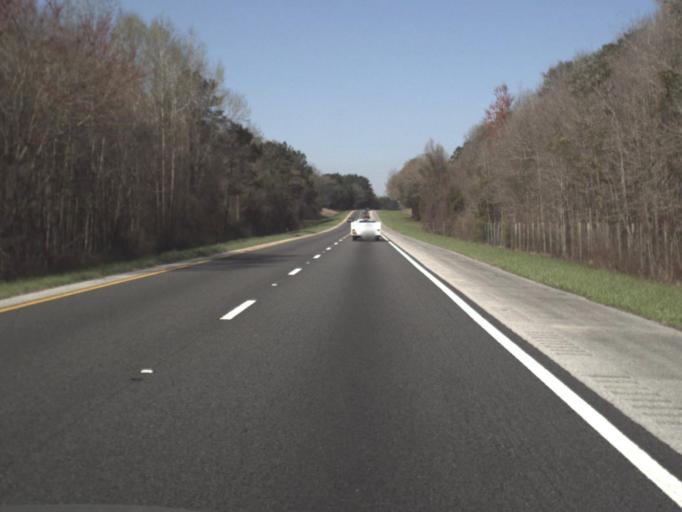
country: US
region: Florida
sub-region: Jackson County
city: Sneads
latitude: 30.6520
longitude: -85.0227
